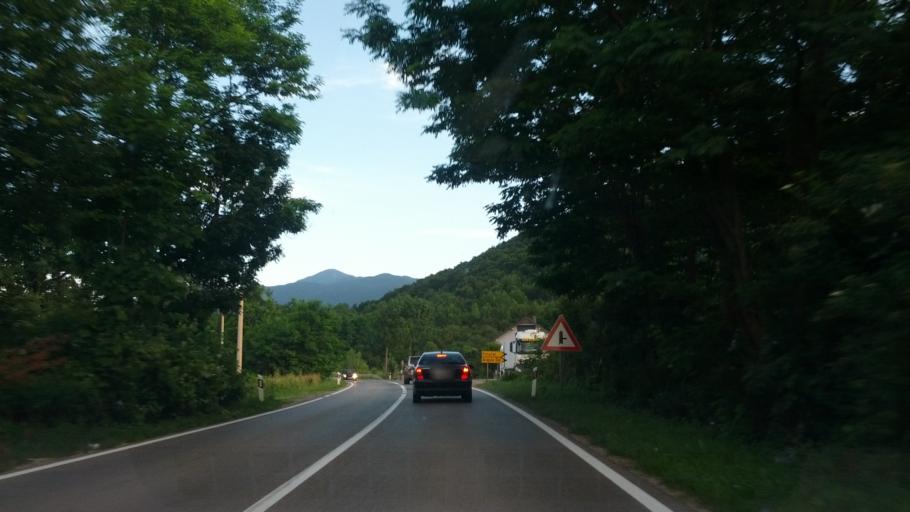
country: BA
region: Federation of Bosnia and Herzegovina
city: Izacic
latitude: 44.8917
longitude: 15.7243
